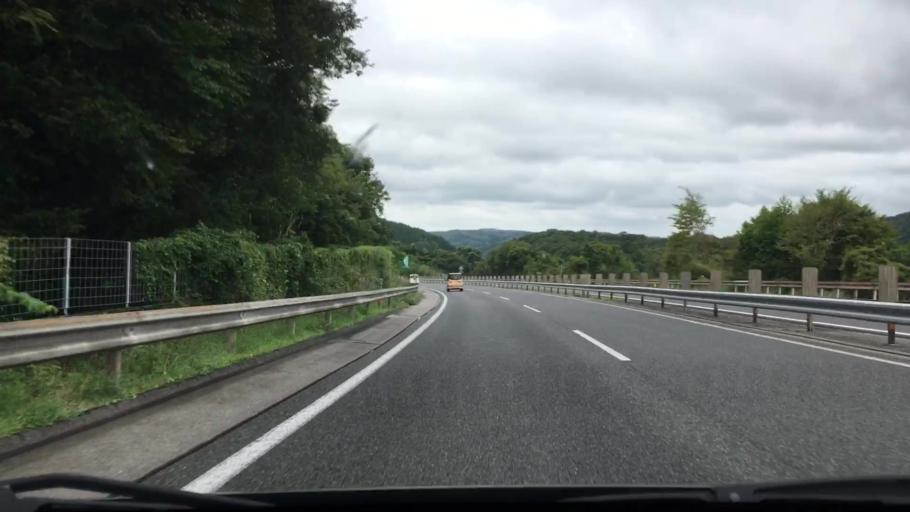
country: JP
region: Hiroshima
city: Miyoshi
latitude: 34.7777
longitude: 132.8401
